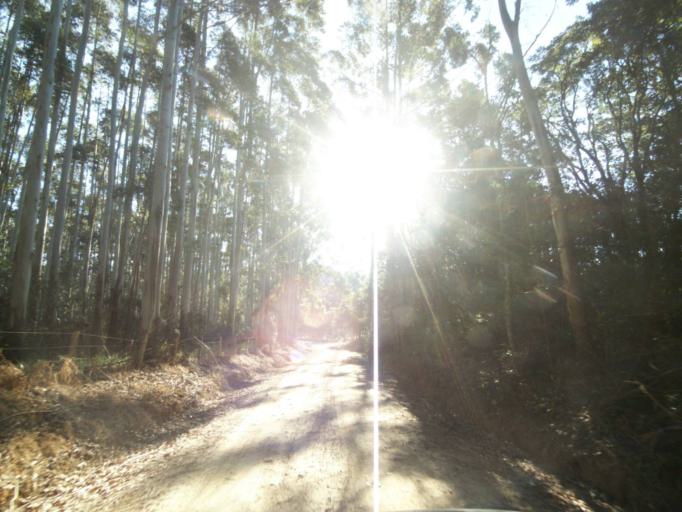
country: BR
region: Parana
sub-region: Telemaco Borba
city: Telemaco Borba
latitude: -24.5116
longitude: -50.6565
